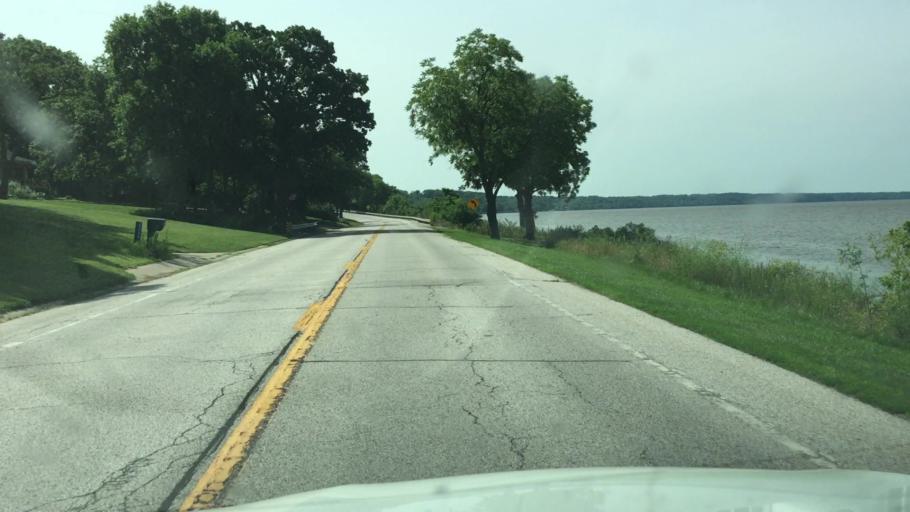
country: US
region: Illinois
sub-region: Hancock County
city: Nauvoo
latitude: 40.5225
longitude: -91.3659
